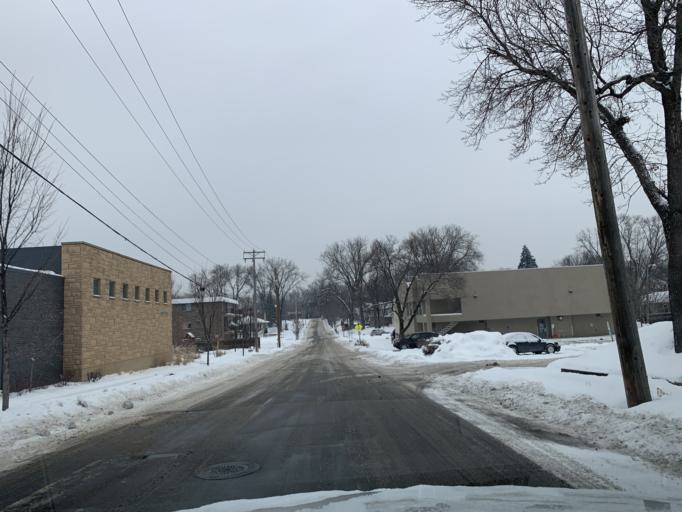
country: US
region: Minnesota
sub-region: Hennepin County
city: Saint Louis Park
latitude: 44.9488
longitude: -93.3339
